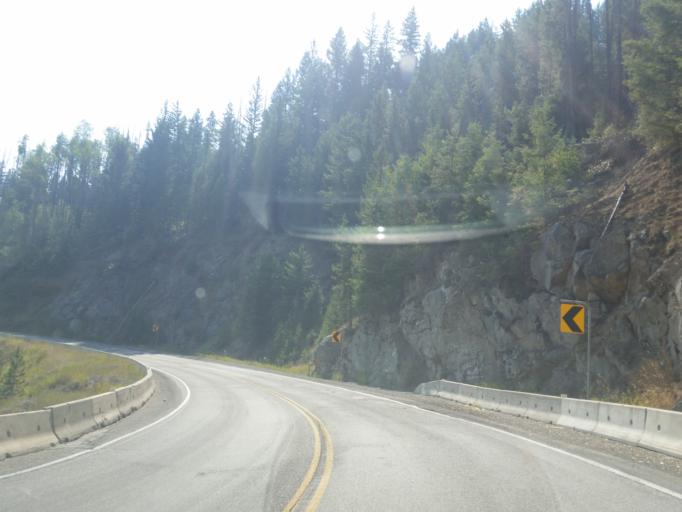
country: CA
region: British Columbia
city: Princeton
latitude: 49.1890
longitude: -120.5619
